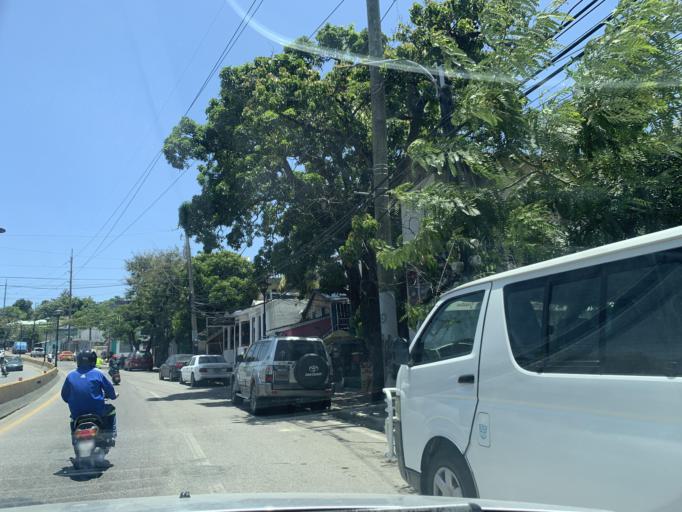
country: DO
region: Puerto Plata
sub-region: Puerto Plata
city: Puerto Plata
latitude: 19.7877
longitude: -70.6961
